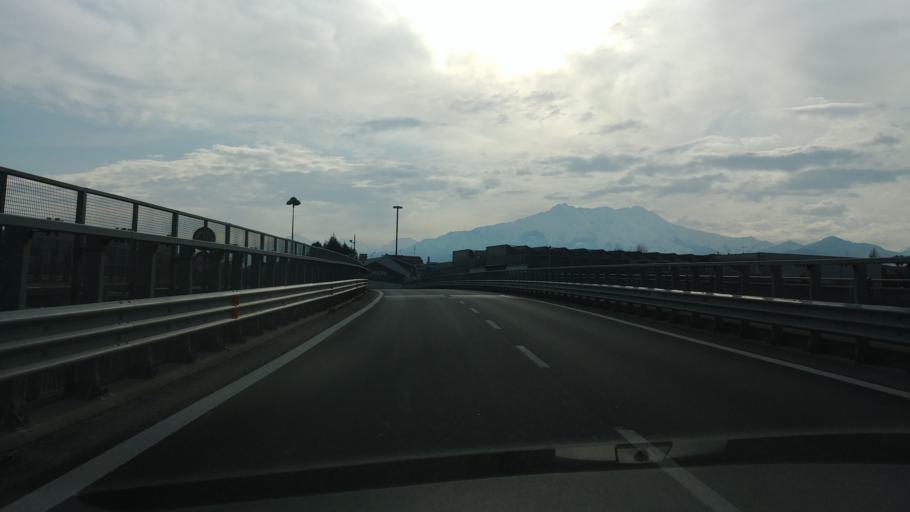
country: IT
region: Piedmont
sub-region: Provincia di Cuneo
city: Cuneo
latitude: 44.3820
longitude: 7.5262
